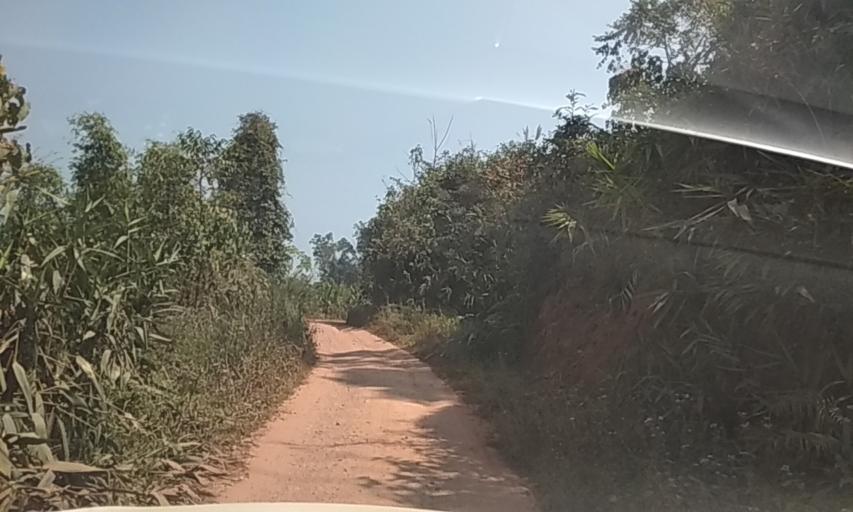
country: CN
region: Yunnan
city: Mengla
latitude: 21.5315
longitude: 101.8308
